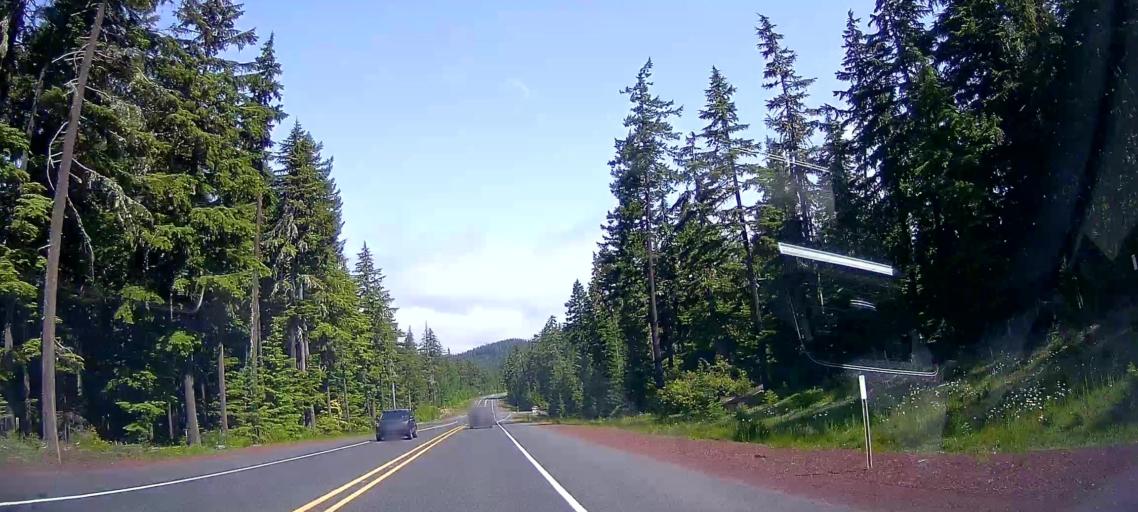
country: US
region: Oregon
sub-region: Clackamas County
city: Mount Hood Village
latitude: 45.1929
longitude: -121.6894
